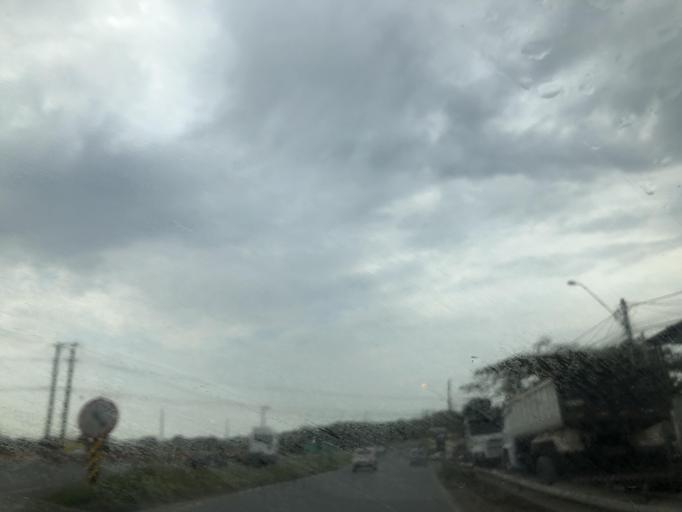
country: BR
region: Sao Paulo
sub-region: Salto De Pirapora
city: Salto de Pirapora
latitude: -23.6427
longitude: -47.5821
